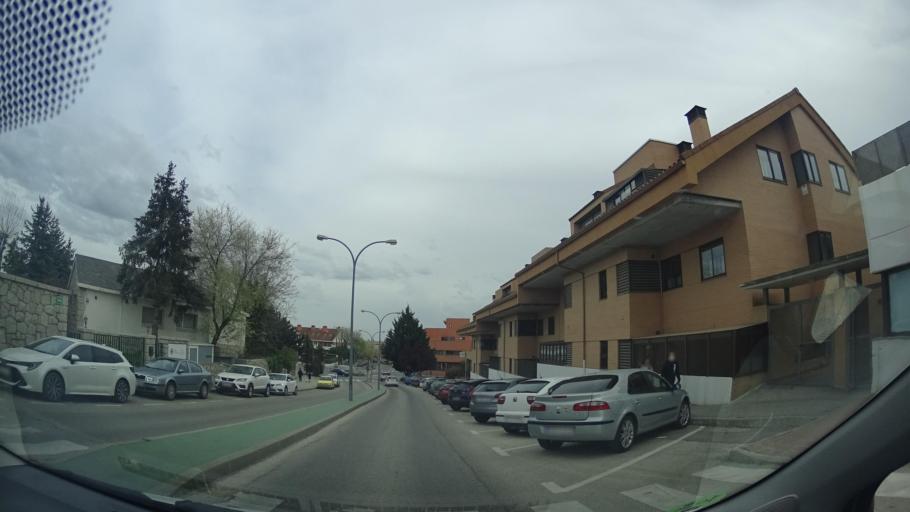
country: ES
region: Madrid
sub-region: Provincia de Madrid
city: Colmenar Viejo
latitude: 40.6617
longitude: -3.7627
